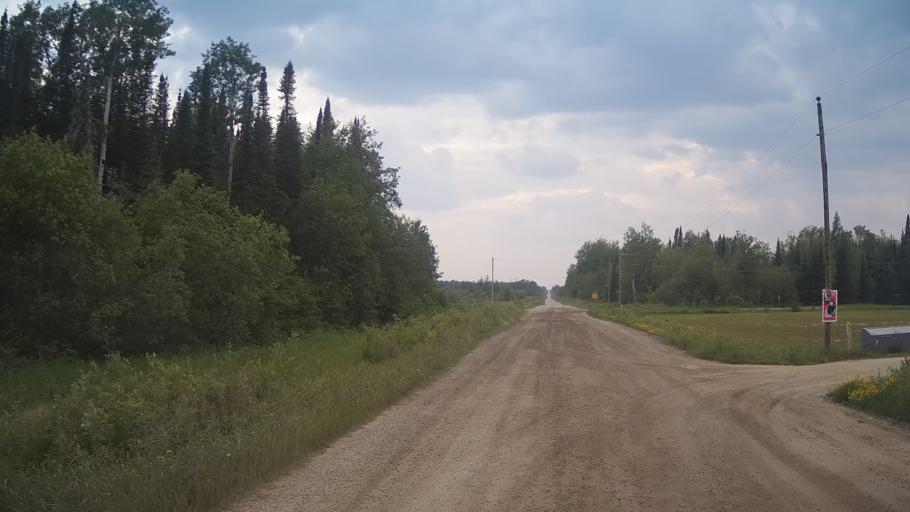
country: CA
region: Ontario
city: Hearst
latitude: 49.6451
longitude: -83.2834
